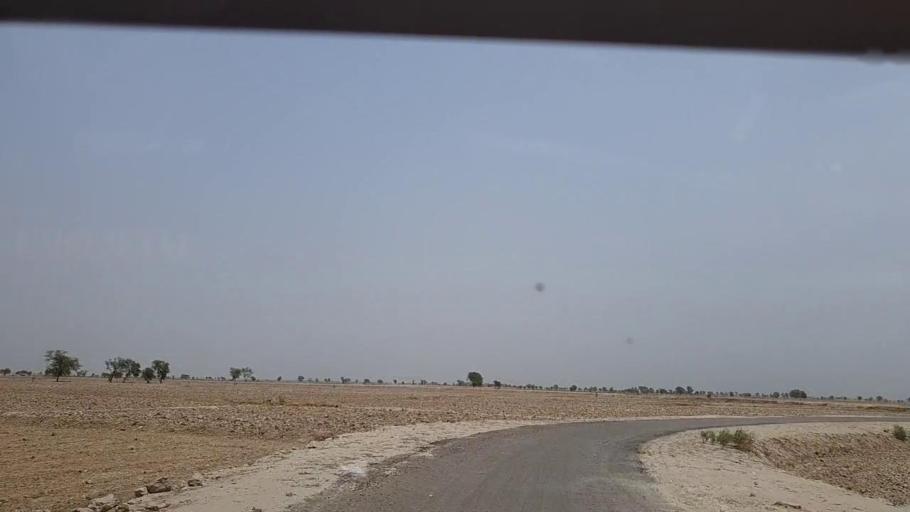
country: PK
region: Sindh
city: Khairpur Nathan Shah
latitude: 27.0144
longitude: 67.6240
